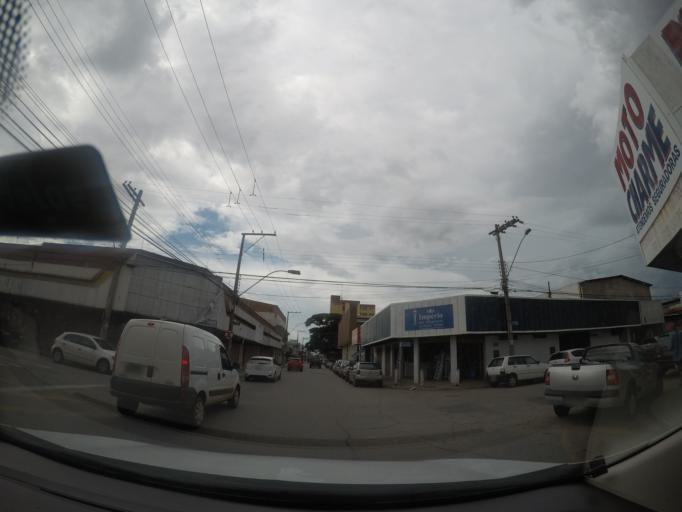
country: BR
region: Goias
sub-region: Goiania
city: Goiania
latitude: -16.6746
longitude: -49.2873
